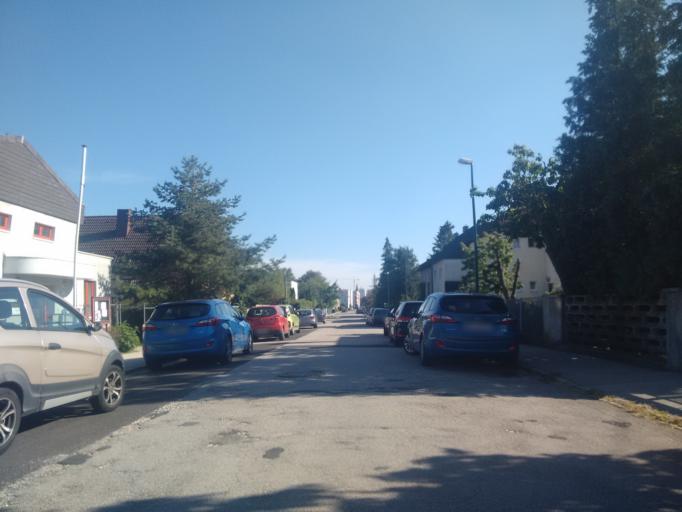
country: AT
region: Upper Austria
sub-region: Wels Stadt
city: Wels
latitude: 48.1704
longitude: 14.0181
